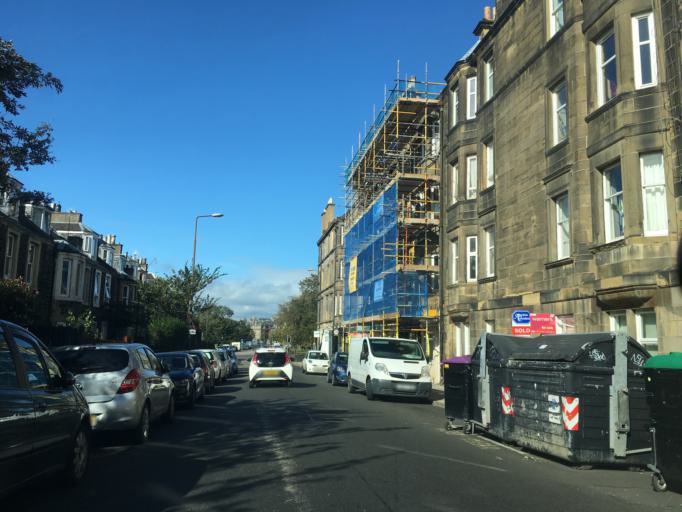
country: GB
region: Scotland
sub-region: West Lothian
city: Seafield
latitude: 55.9691
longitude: -3.1592
